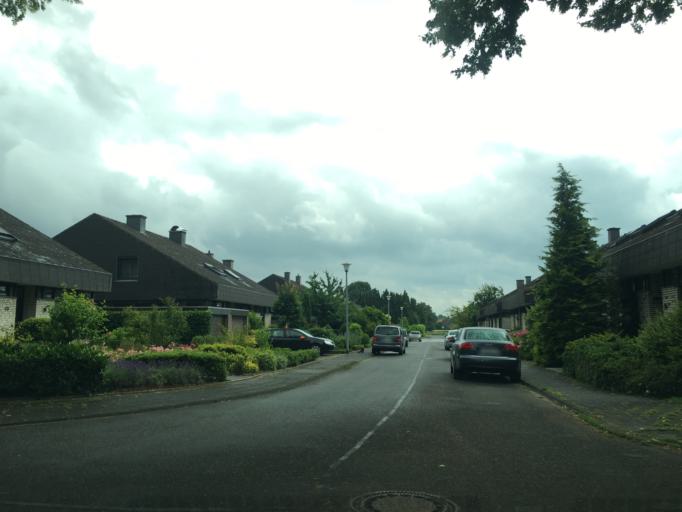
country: DE
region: North Rhine-Westphalia
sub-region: Regierungsbezirk Munster
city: Greven
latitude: 52.0352
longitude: 7.6185
